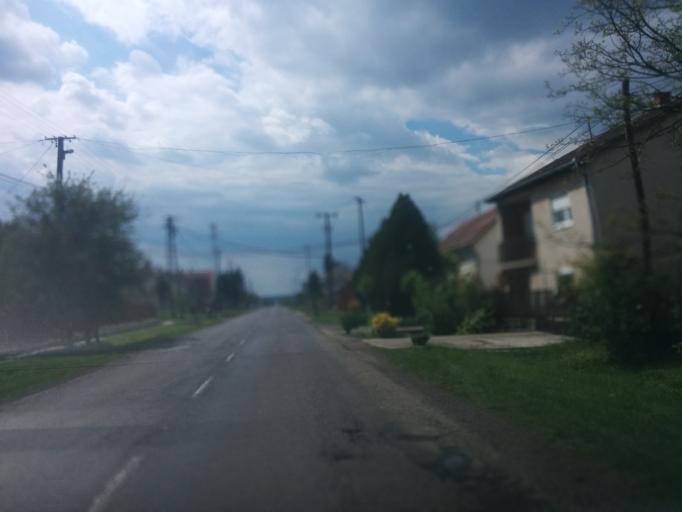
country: HU
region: Nograd
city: Jobbagyi
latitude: 47.8296
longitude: 19.6697
